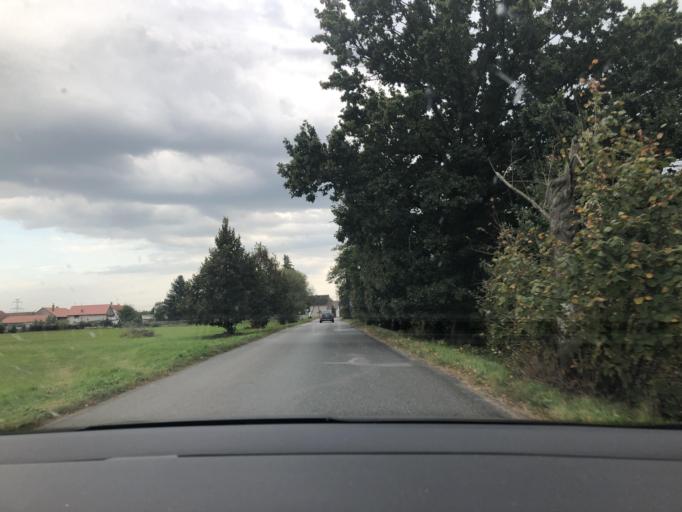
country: CZ
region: Pardubicky
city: Chvaletice
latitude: 50.0521
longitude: 15.4403
